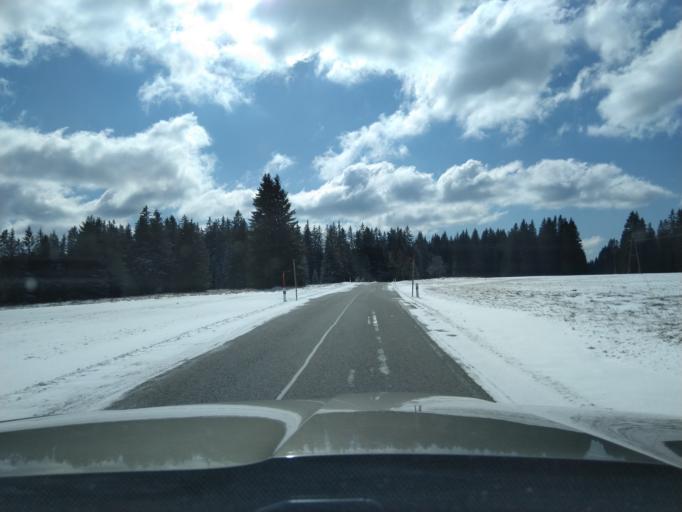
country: CZ
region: Jihocesky
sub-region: Okres Prachatice
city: Borova Lada
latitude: 49.0442
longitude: 13.5782
